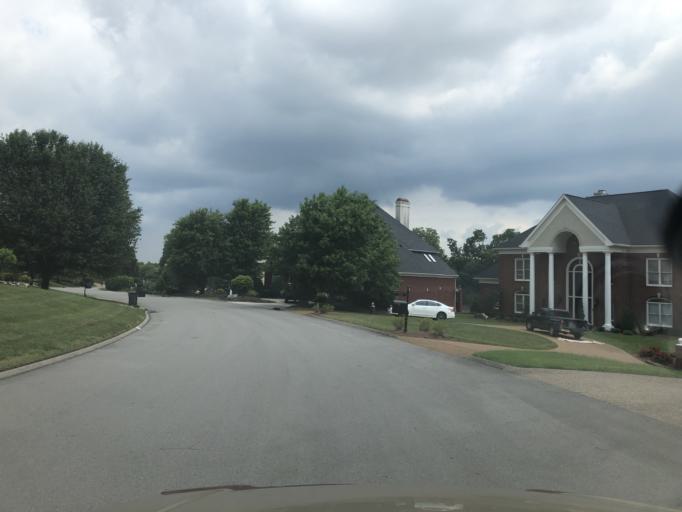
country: US
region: Tennessee
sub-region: Davidson County
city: Lakewood
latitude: 36.2379
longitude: -86.6032
